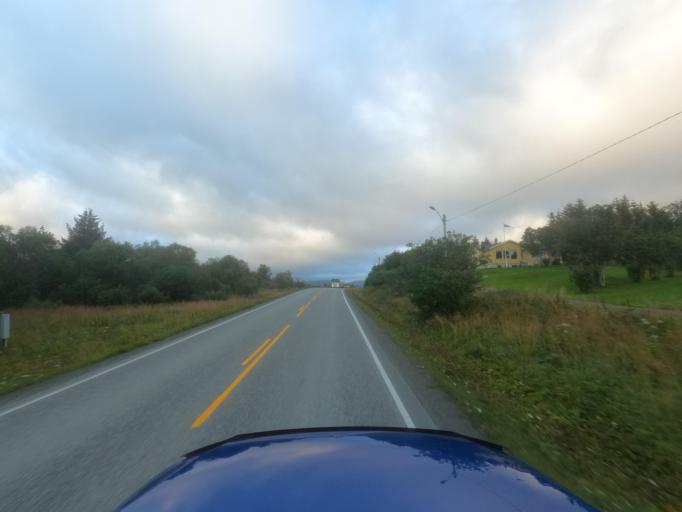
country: NO
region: Nordland
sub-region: Vestvagoy
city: Evjen
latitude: 68.2192
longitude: 13.7248
